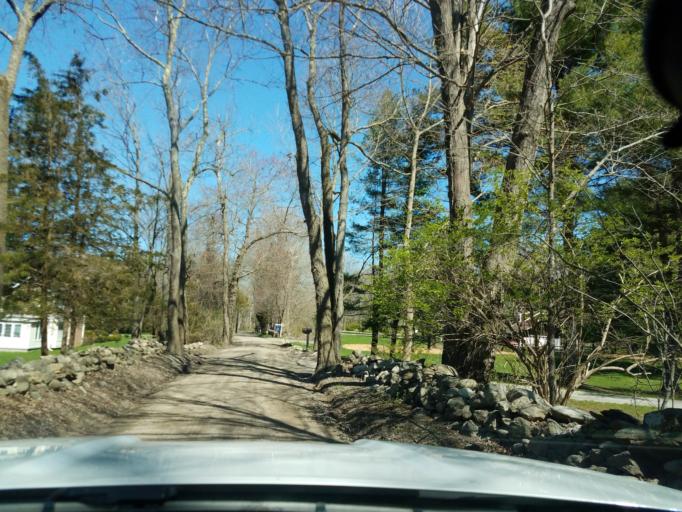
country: US
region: Connecticut
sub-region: Fairfield County
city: Georgetown
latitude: 41.2228
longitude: -73.3821
